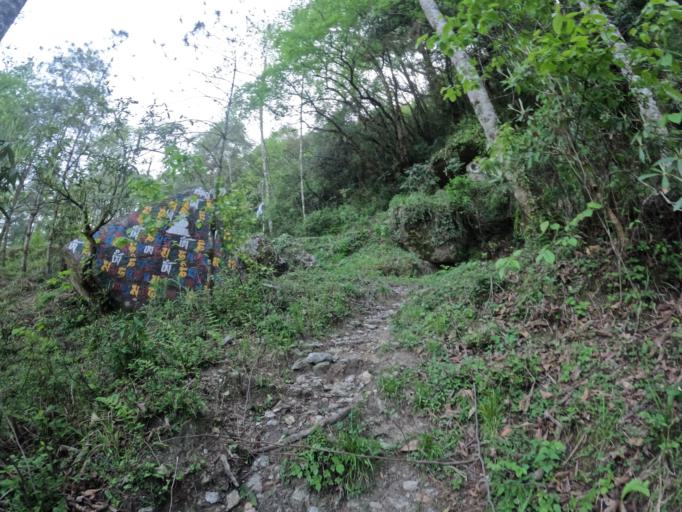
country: NP
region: Eastern Region
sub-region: Sagarmatha Zone
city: Namche Bazar
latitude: 27.4884
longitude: 86.5816
